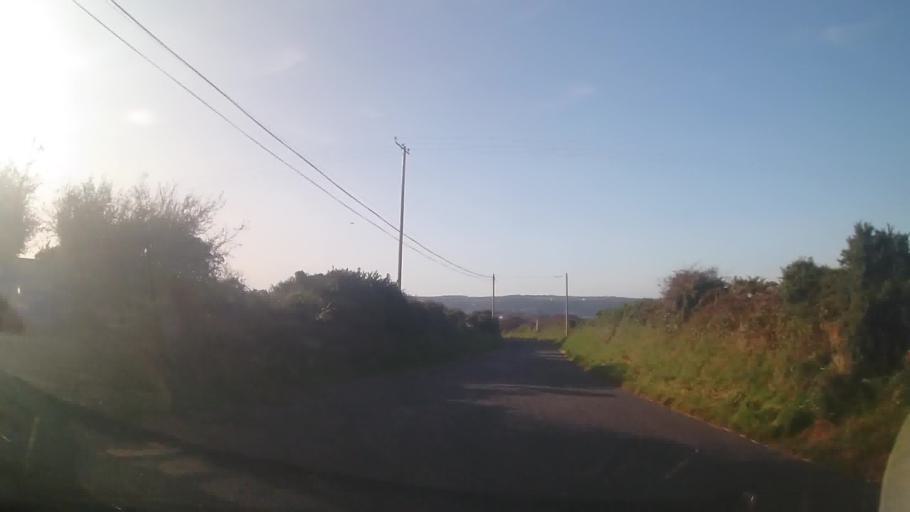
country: GB
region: Wales
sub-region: Pembrokeshire
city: Fishguard
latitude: 51.9887
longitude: -4.9627
